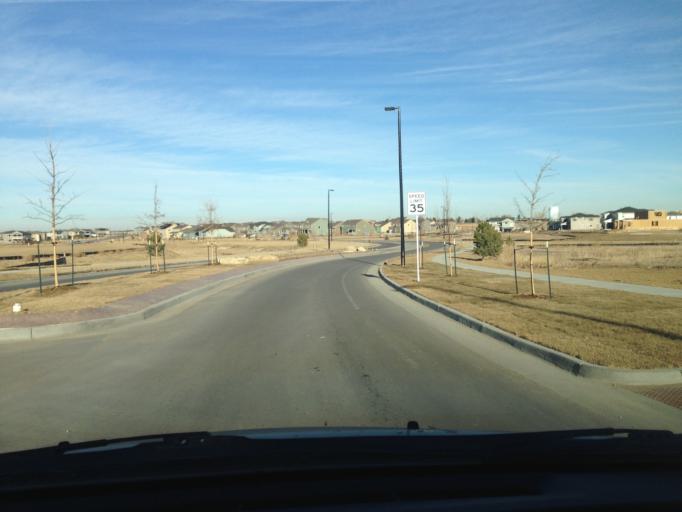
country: US
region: Colorado
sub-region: Boulder County
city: Lafayette
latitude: 40.0227
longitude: -105.0903
